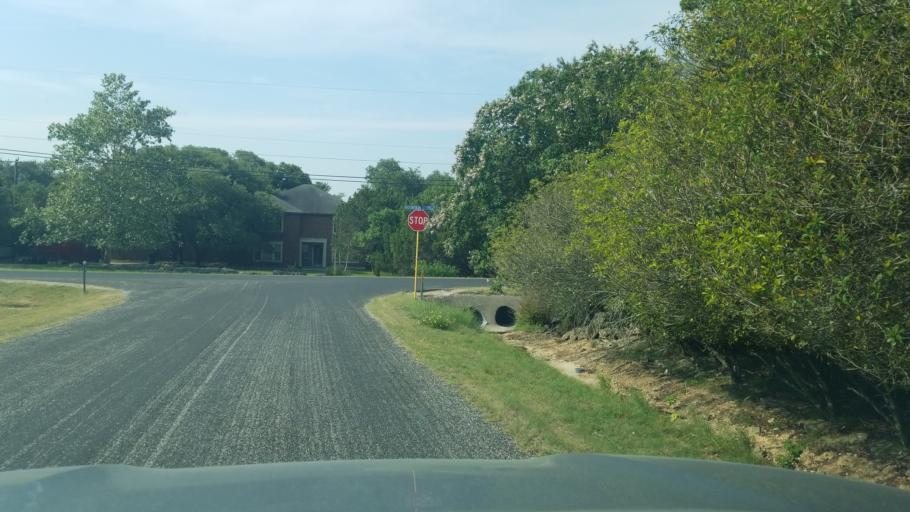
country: US
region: Texas
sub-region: Bexar County
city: Timberwood Park
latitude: 29.7001
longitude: -98.4954
